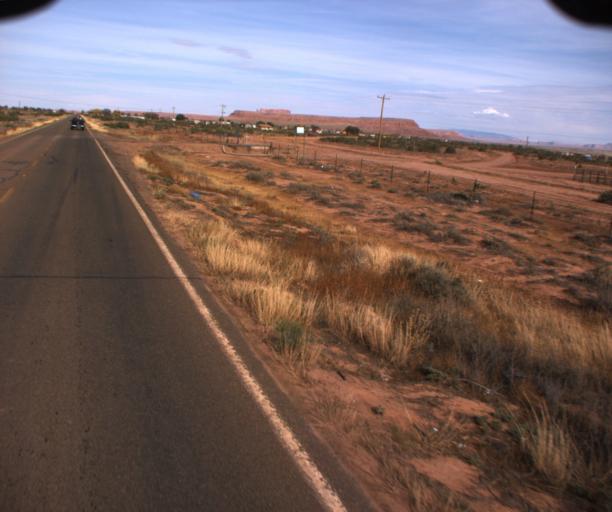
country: US
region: Arizona
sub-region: Apache County
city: Many Farms
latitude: 36.3998
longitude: -109.6091
